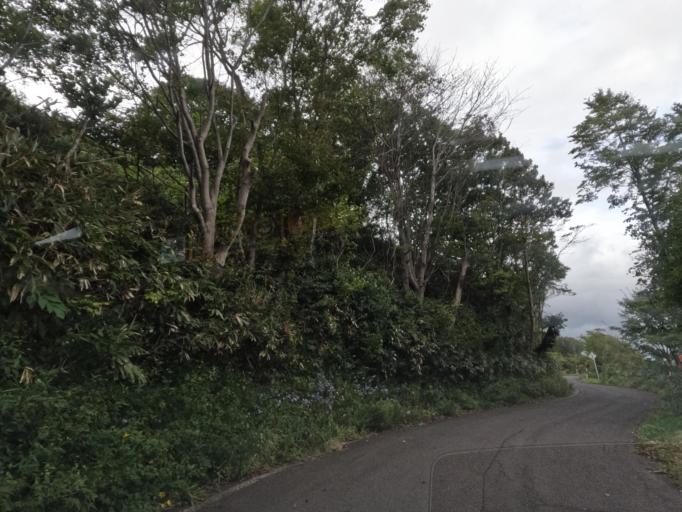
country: JP
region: Hokkaido
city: Muroran
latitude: 42.3286
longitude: 141.0030
